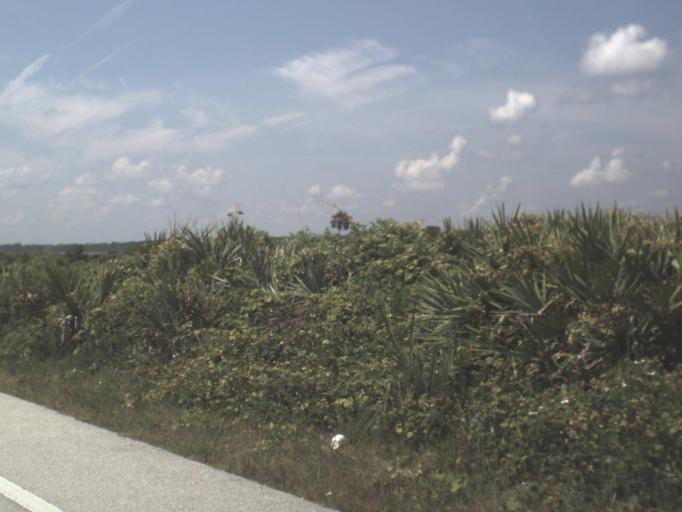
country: US
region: Florida
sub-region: Saint Johns County
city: Palm Valley
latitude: 30.1149
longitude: -81.3453
